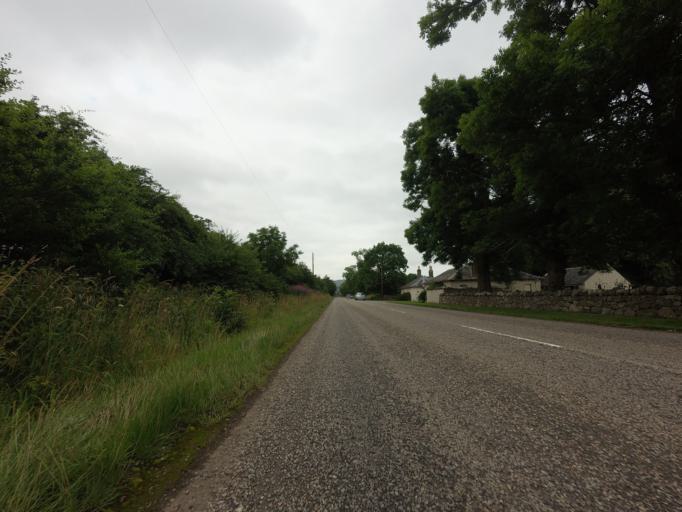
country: GB
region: Scotland
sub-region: Highland
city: Alness
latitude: 57.9134
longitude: -4.3806
